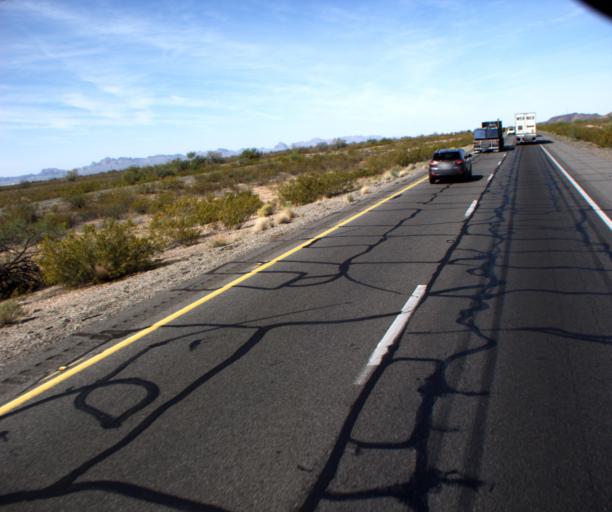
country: US
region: Arizona
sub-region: Maricopa County
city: Buckeye
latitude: 33.5150
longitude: -113.0351
